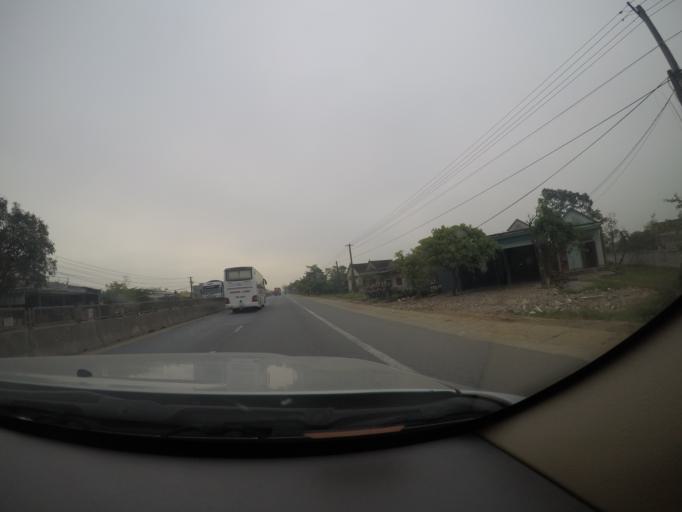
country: VN
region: Ha Tinh
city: Cam Xuyen
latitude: 18.2153
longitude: 106.0963
